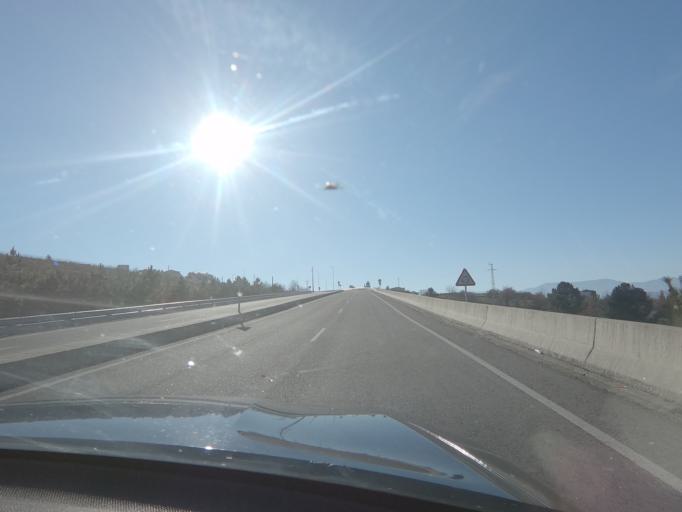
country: PT
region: Vila Real
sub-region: Vila Real
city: Vila Real
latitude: 41.2872
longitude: -7.7272
